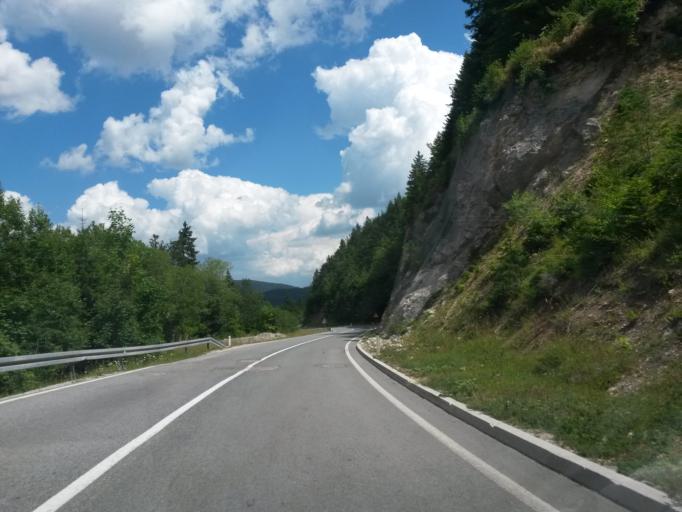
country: BA
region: Federation of Bosnia and Herzegovina
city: Bugojno
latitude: 44.0230
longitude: 17.2971
